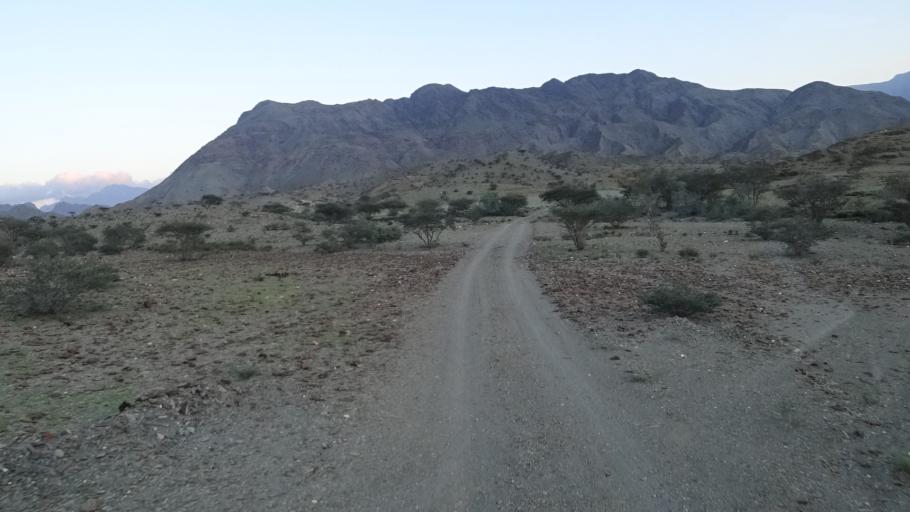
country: OM
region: Al Batinah
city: Rustaq
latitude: 23.2754
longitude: 57.3603
